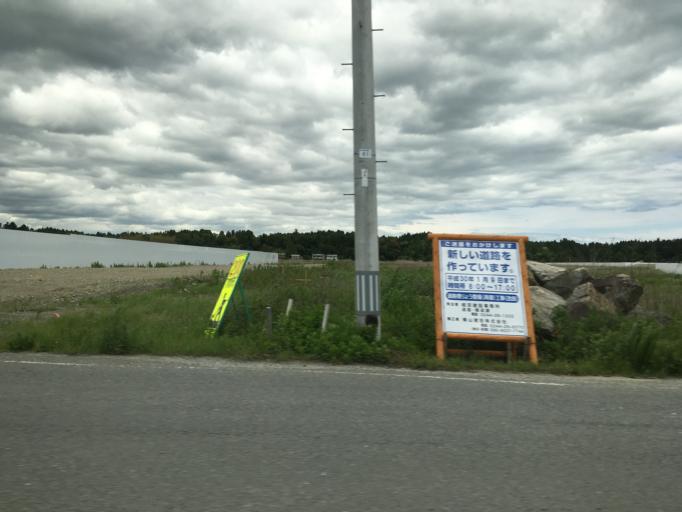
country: JP
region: Fukushima
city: Namie
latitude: 37.4923
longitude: 141.0289
